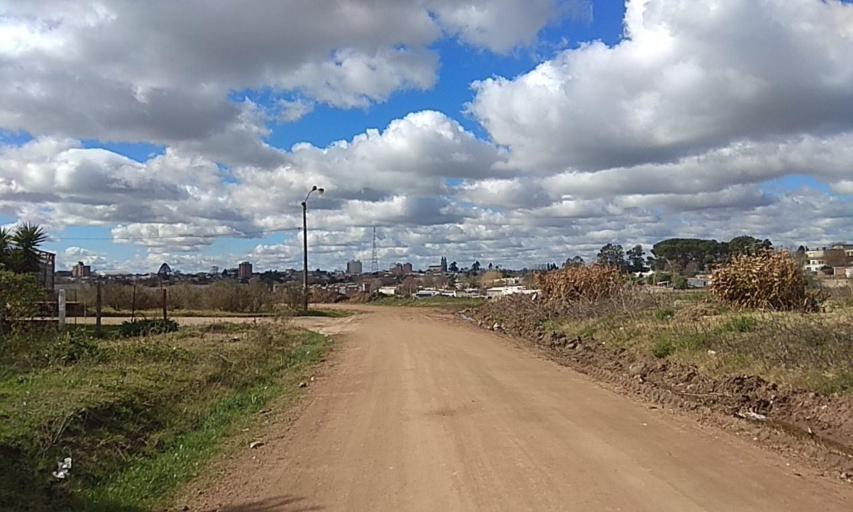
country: UY
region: Florida
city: Florida
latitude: -34.0956
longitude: -56.2308
